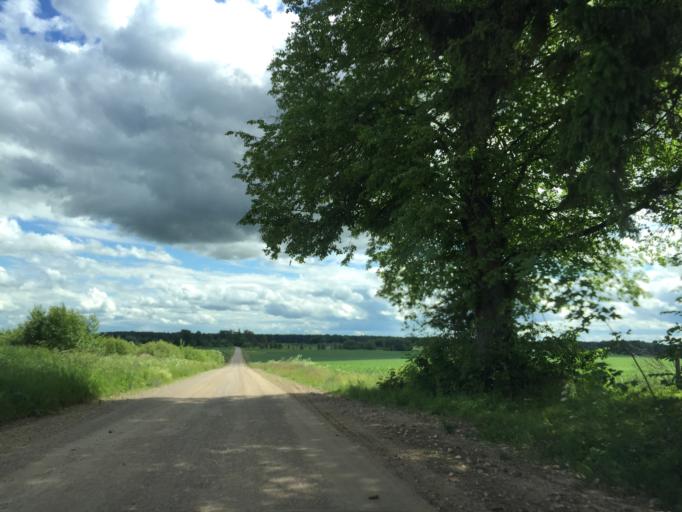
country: LV
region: Vecumnieki
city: Vecumnieki
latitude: 56.4793
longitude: 24.4164
